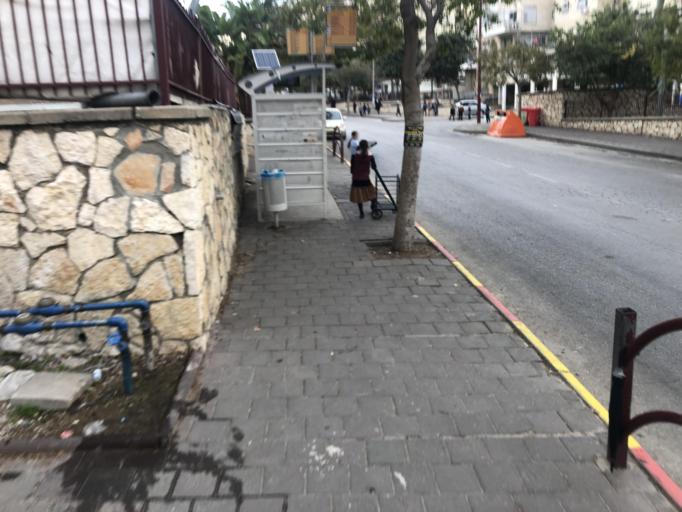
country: IL
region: Jerusalem
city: Modiin Ilit
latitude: 31.9373
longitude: 35.0434
